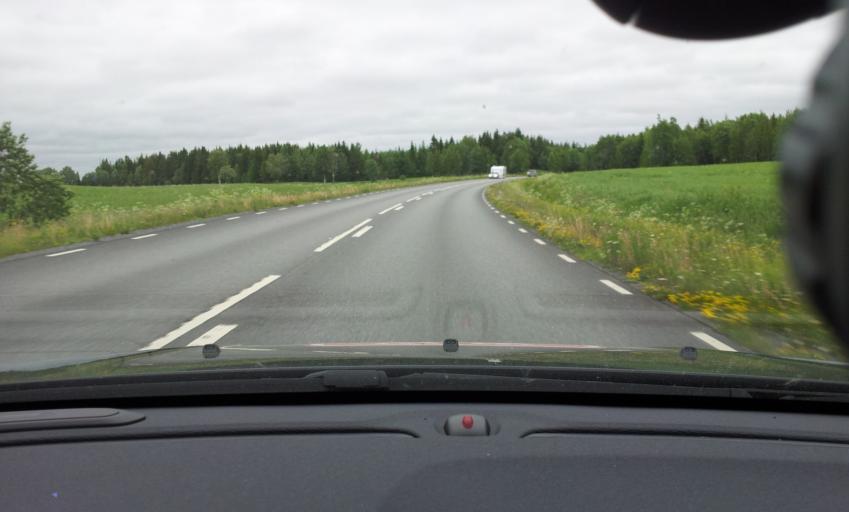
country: SE
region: Jaemtland
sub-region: Krokoms Kommun
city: Krokom
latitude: 63.0773
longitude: 14.2925
